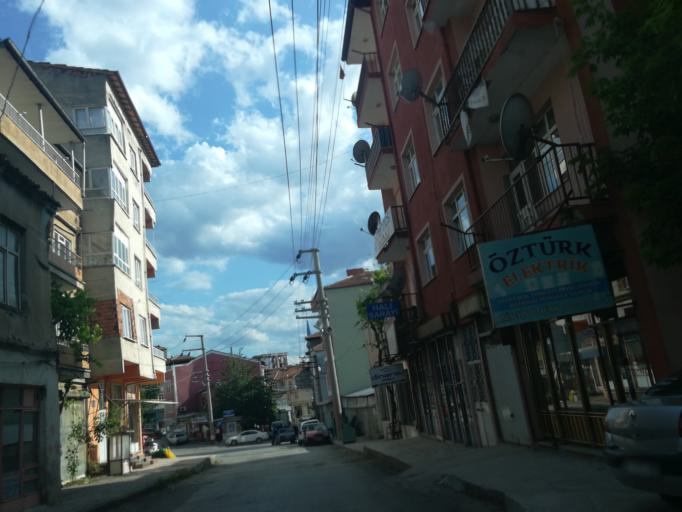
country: TR
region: Afyonkarahisar
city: Dinar
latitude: 38.0693
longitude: 30.1677
